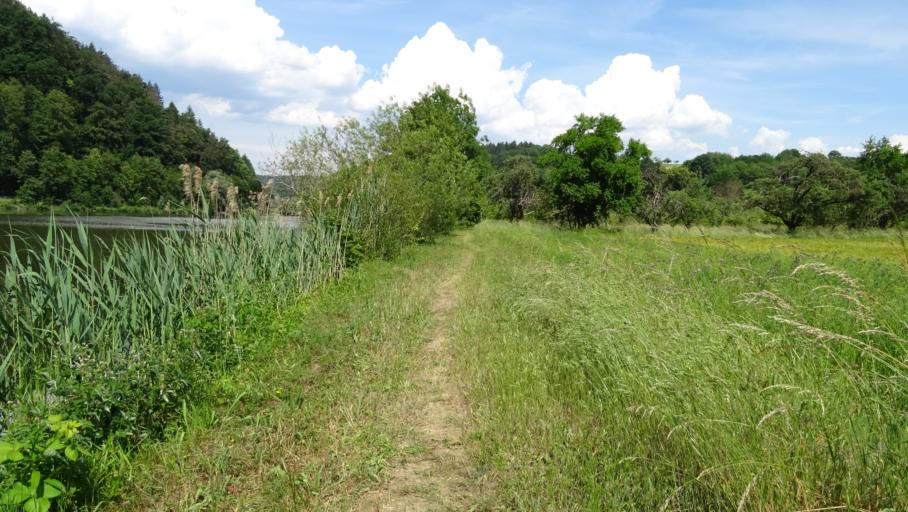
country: DE
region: Baden-Wuerttemberg
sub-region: Karlsruhe Region
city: Binau
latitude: 49.3719
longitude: 9.0553
